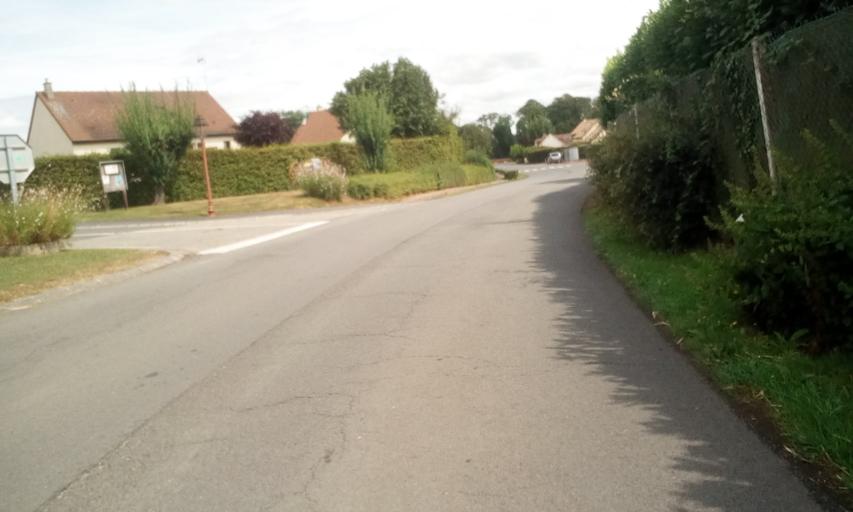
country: FR
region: Lower Normandy
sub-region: Departement du Calvados
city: Bavent
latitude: 49.2420
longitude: -0.1817
